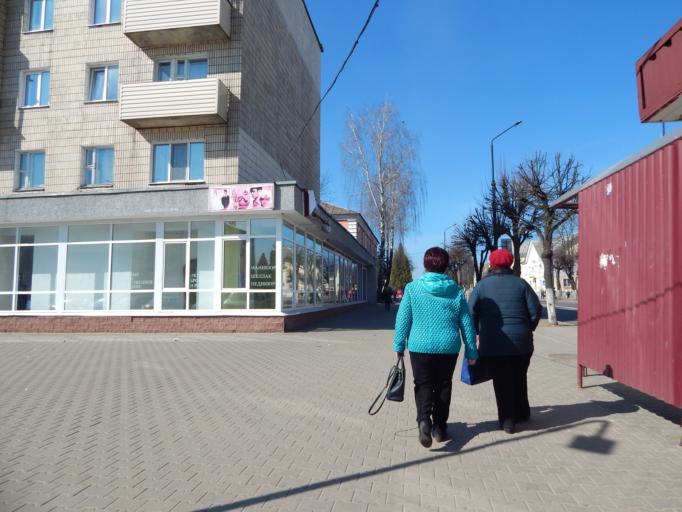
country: BY
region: Minsk
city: Horad Barysaw
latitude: 54.2219
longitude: 28.5219
